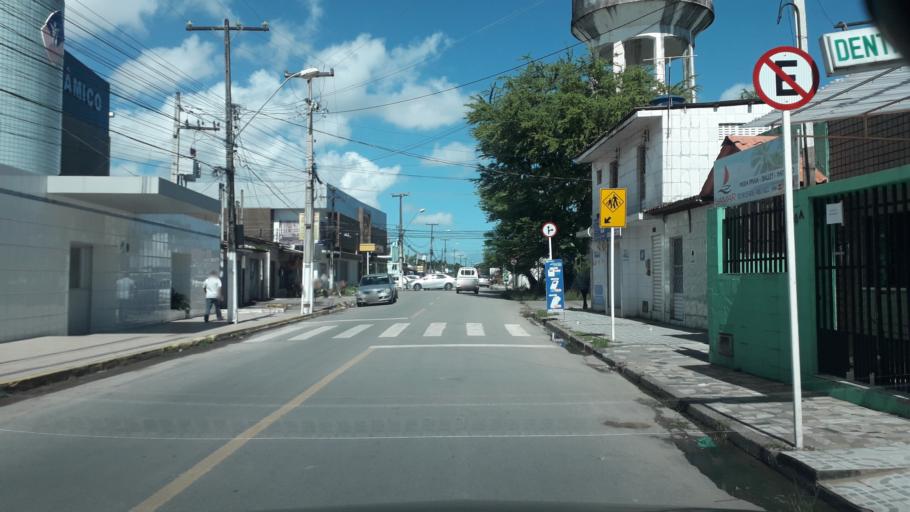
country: BR
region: Alagoas
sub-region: Satuba
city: Satuba
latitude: -9.5777
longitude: -35.7716
